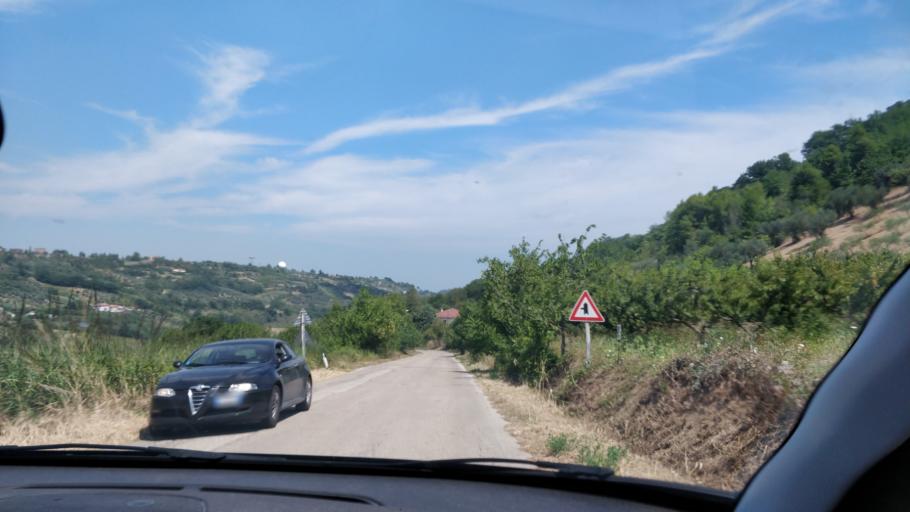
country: IT
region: Abruzzo
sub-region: Provincia di Chieti
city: Torrevecchia
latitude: 42.4027
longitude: 14.2056
